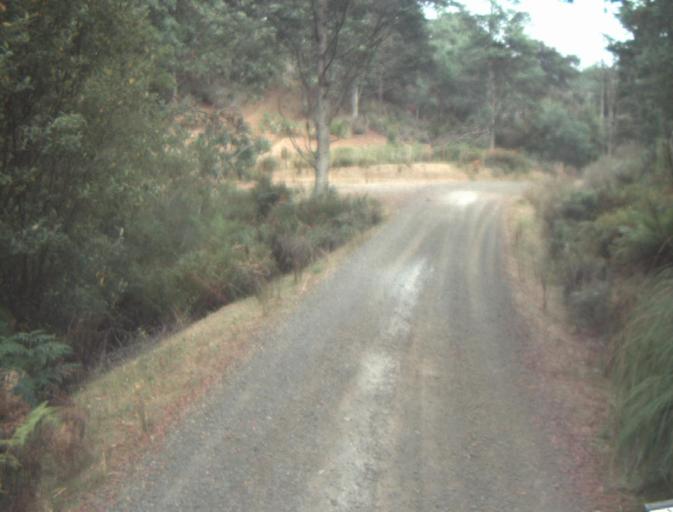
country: AU
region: Tasmania
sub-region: Launceston
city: Mayfield
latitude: -41.2819
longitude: 147.2340
